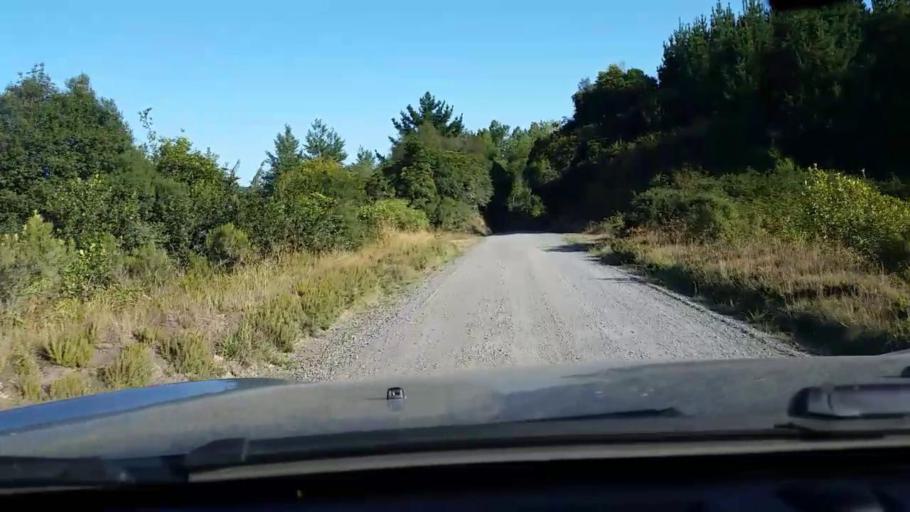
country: NZ
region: Waikato
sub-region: Taupo District
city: Taupo
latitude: -38.4562
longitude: 176.1571
